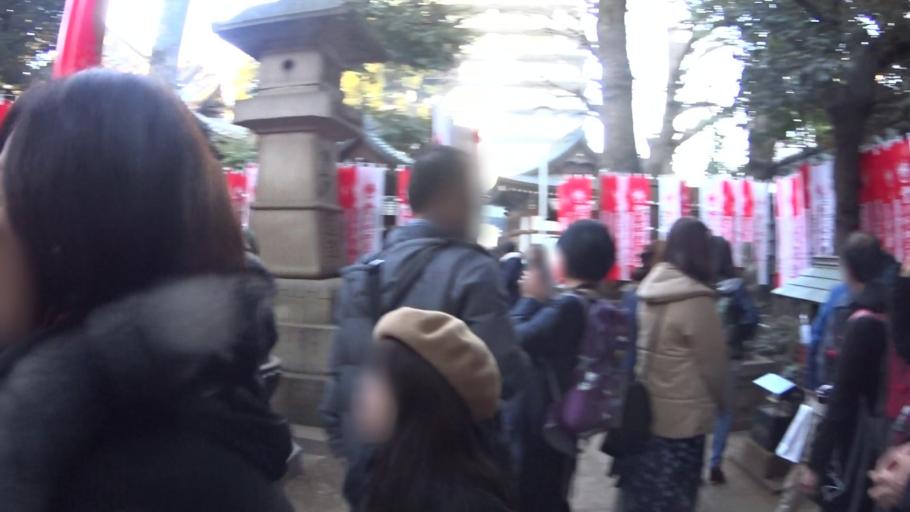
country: JP
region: Tokyo
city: Tokyo
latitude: 35.6745
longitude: 139.7326
